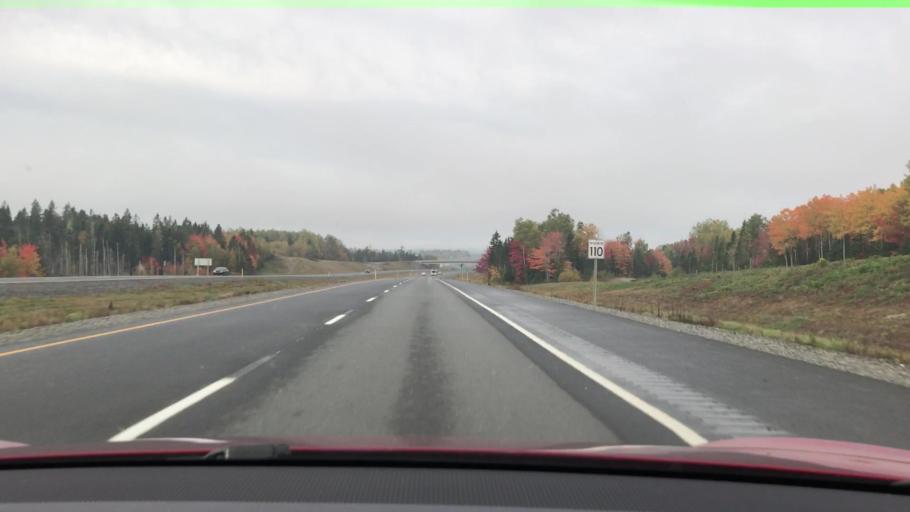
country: US
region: Maine
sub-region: Washington County
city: Calais
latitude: 45.2191
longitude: -67.2299
